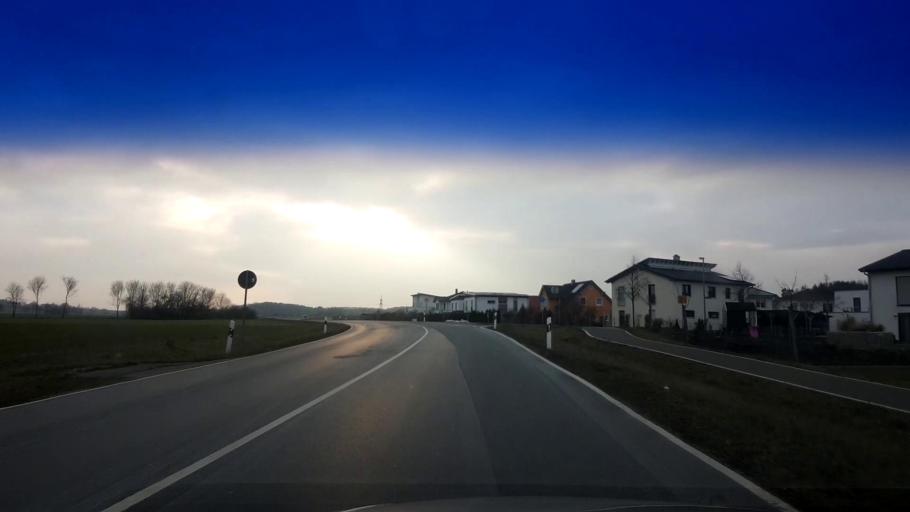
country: DE
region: Bavaria
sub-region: Upper Franconia
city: Hirschaid
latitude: 49.7990
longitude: 10.9707
